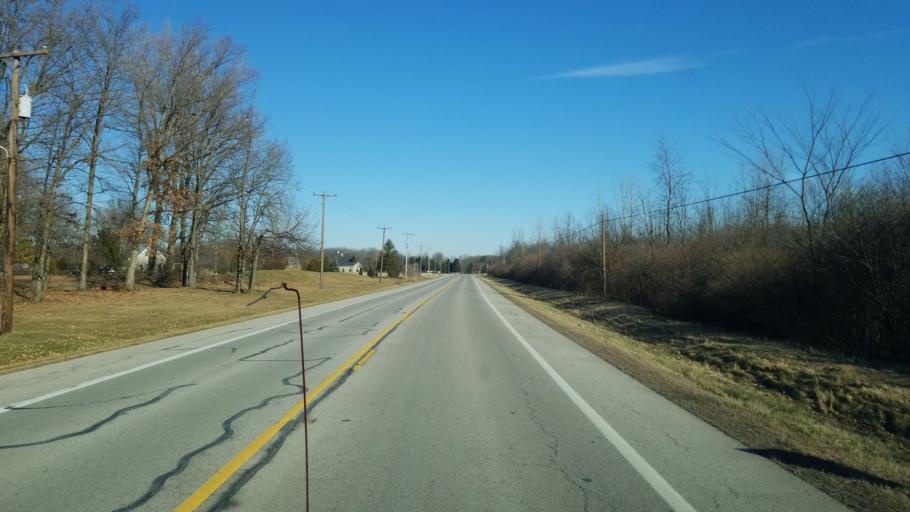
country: US
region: Ohio
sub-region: Wood County
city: Weston
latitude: 41.4241
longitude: -83.8530
